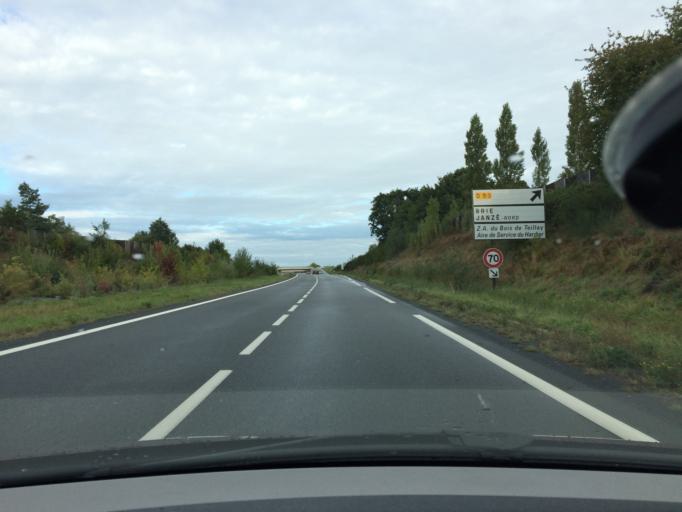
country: FR
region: Brittany
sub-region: Departement d'Ille-et-Vilaine
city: Janze
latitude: 47.9682
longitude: -1.5312
